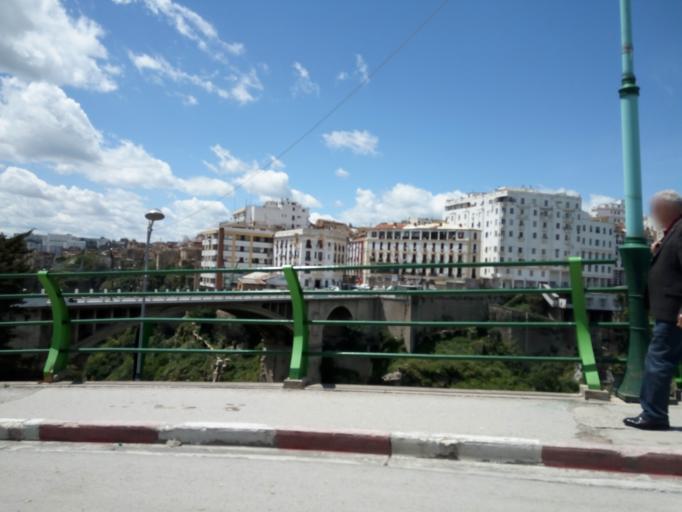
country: DZ
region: Constantine
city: Constantine
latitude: 36.3697
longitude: 6.6190
